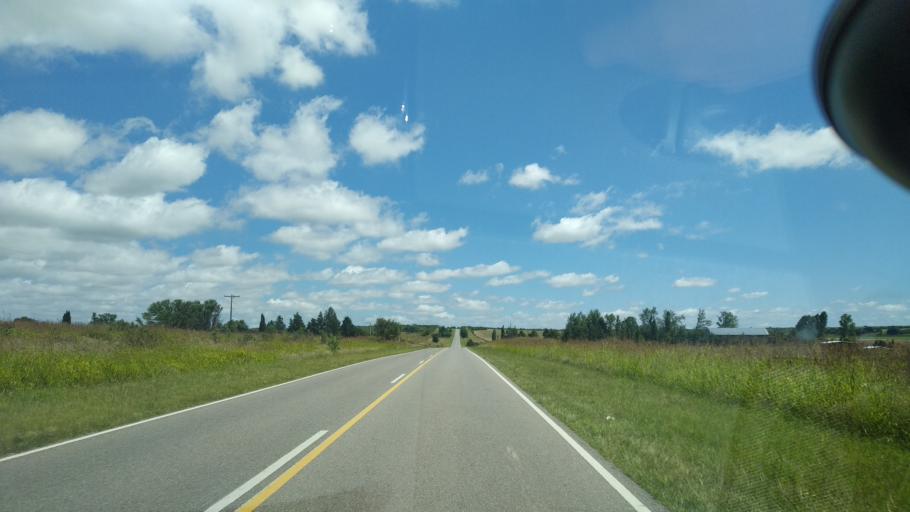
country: AR
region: Cordoba
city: Villa Cura Brochero
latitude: -31.6402
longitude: -65.1030
